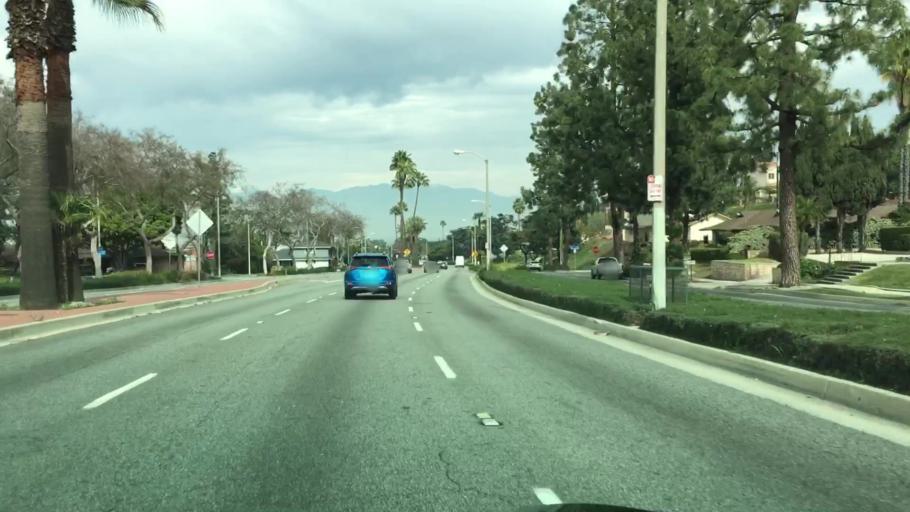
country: US
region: California
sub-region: Los Angeles County
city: Hacienda Heights
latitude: 33.9831
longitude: -117.9727
